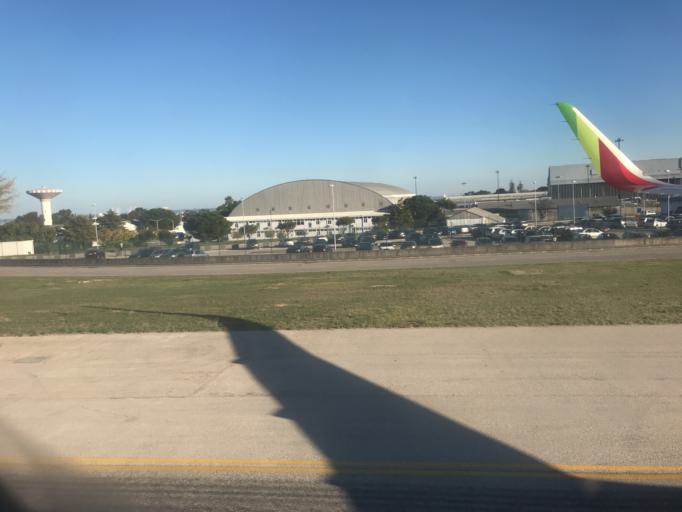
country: PT
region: Lisbon
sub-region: Loures
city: Camarate
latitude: 38.7822
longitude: -9.1330
